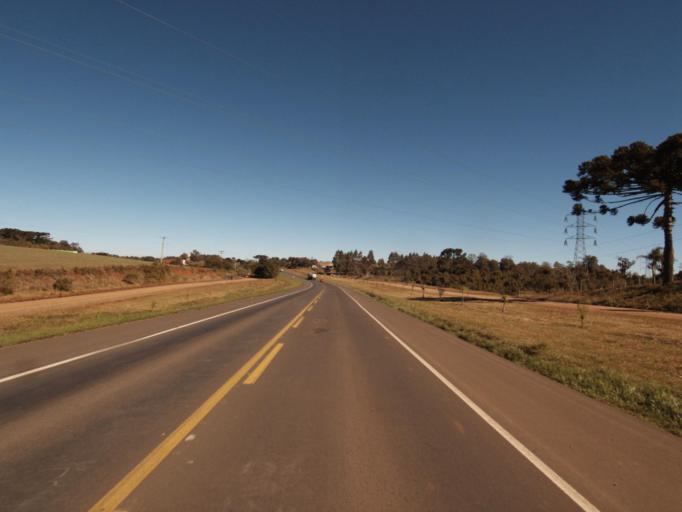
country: BR
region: Santa Catarina
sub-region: Xanxere
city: Xanxere
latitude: -26.8634
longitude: -52.2704
